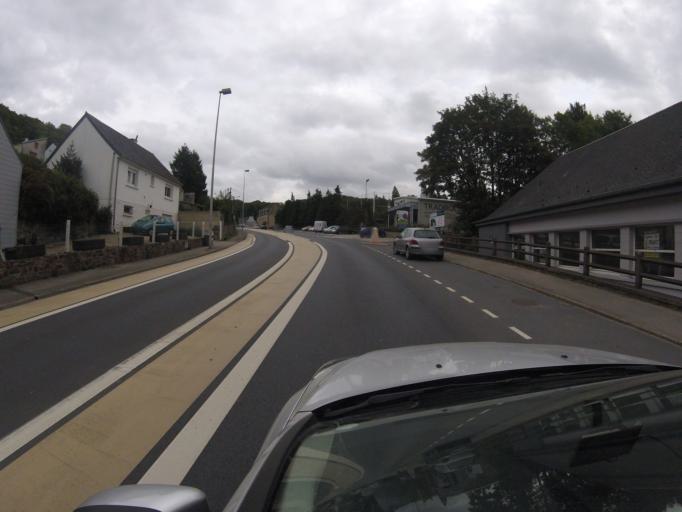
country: FR
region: Lower Normandy
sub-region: Departement de la Manche
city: Cherbourg-Octeville
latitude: 49.6238
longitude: -1.6154
